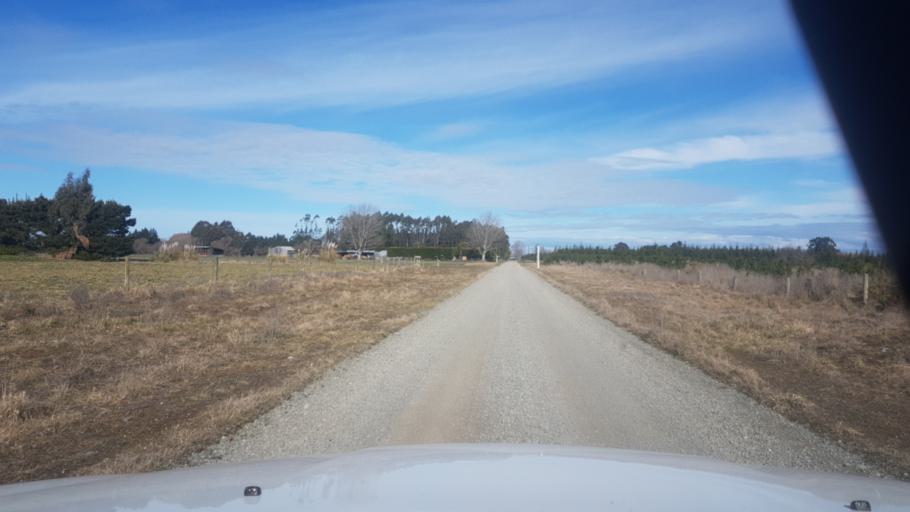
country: NZ
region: Canterbury
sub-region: Timaru District
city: Pleasant Point
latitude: -44.1353
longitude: 171.2782
